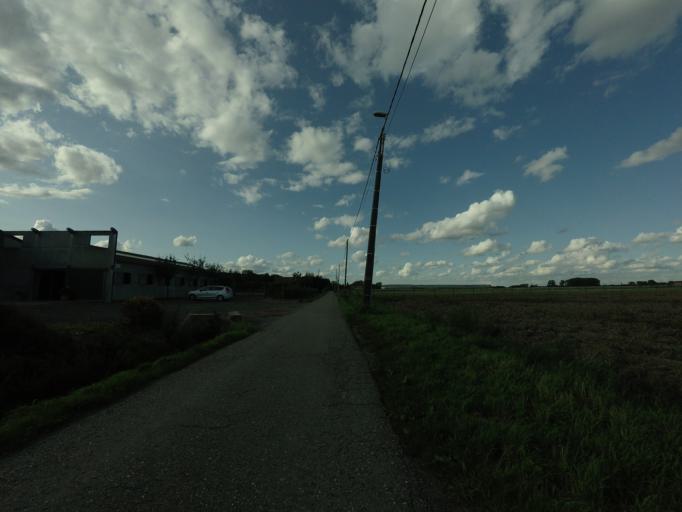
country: BE
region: Flanders
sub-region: Provincie Vlaams-Brabant
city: Kapelle-op-den-Bos
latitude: 50.9863
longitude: 4.3387
